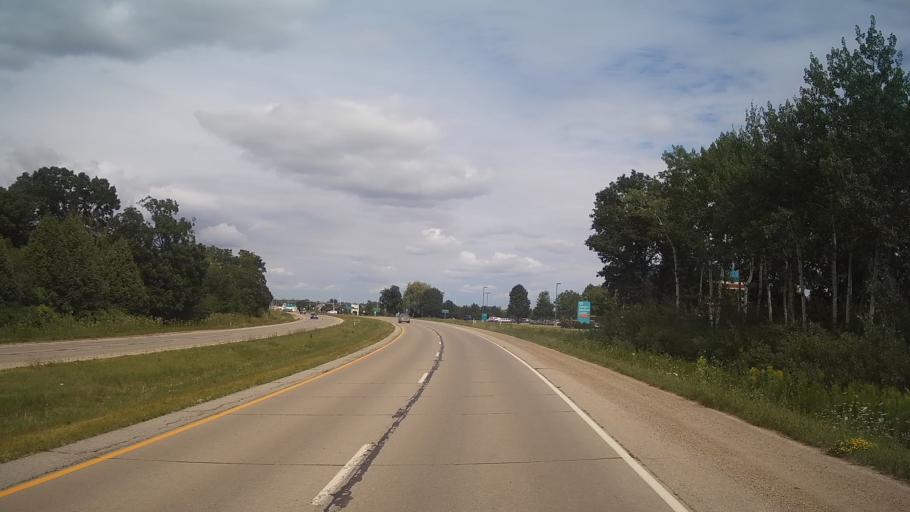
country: US
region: Wisconsin
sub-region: Winnebago County
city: Oshkosh
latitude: 44.0285
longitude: -88.5987
